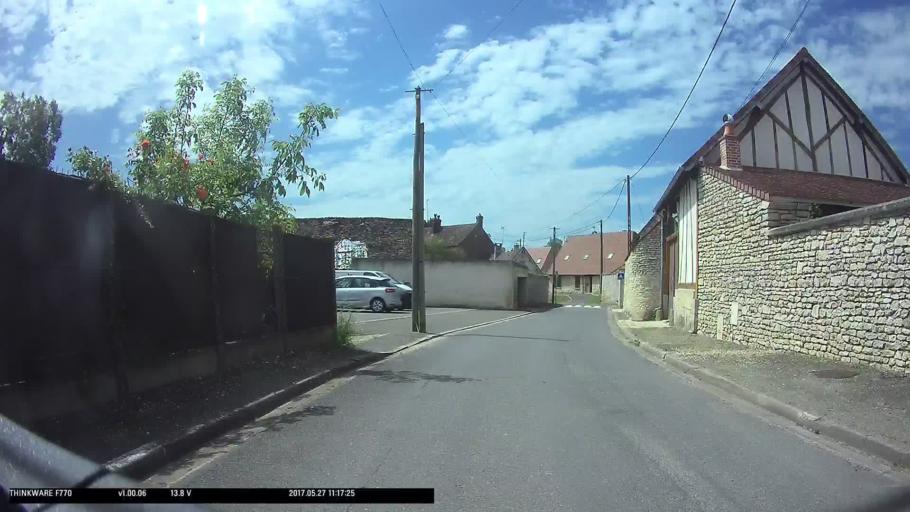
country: FR
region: Picardie
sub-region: Departement de l'Oise
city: Trie-Chateau
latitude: 49.2906
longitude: 1.8334
